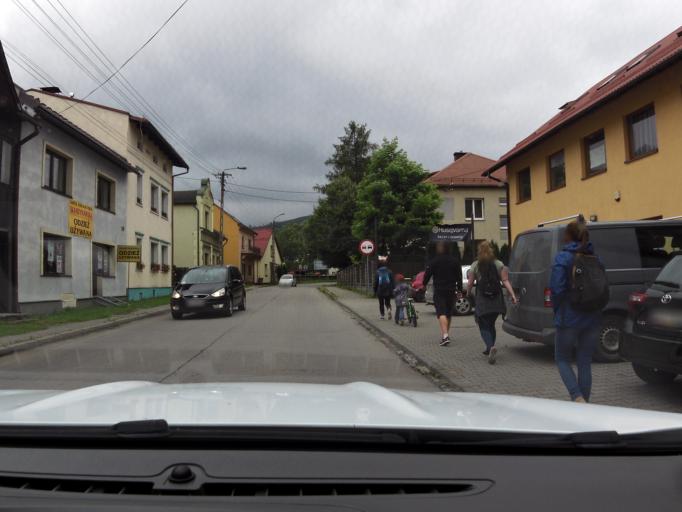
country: PL
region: Silesian Voivodeship
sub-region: Powiat zywiecki
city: Rajcza
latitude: 49.5025
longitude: 19.1015
